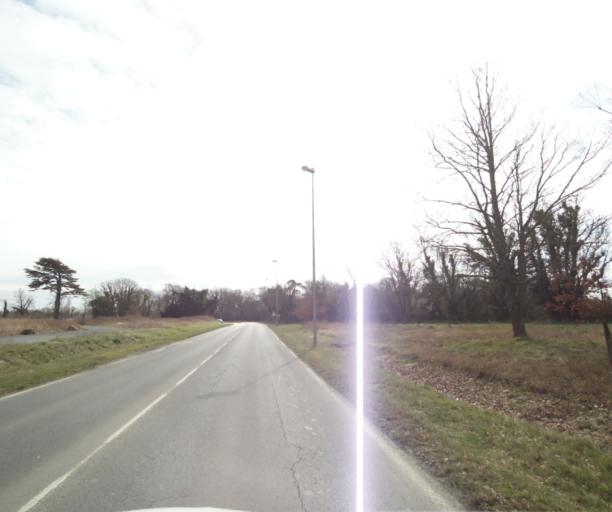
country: FR
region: Poitou-Charentes
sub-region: Departement de la Charente-Maritime
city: Lagord
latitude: 46.1835
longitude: -1.1742
